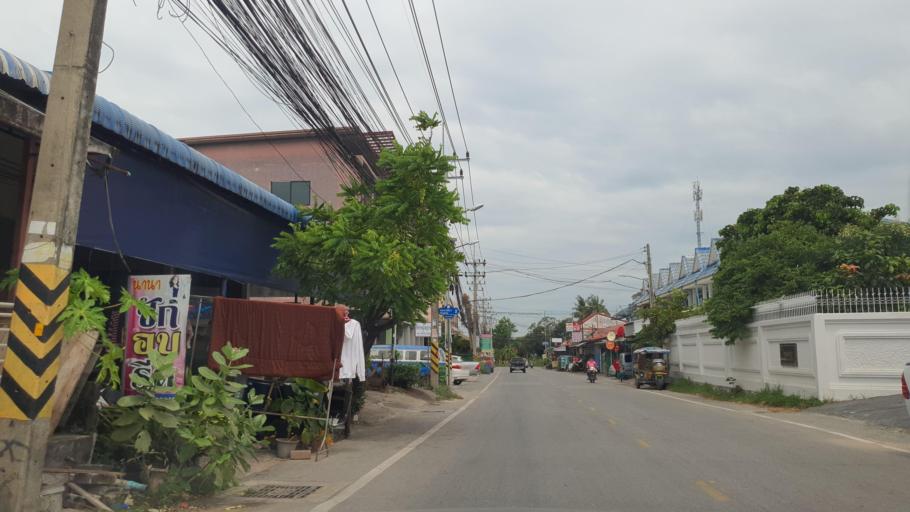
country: TH
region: Chon Buri
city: Bang Lamung
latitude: 12.9834
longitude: 100.9396
